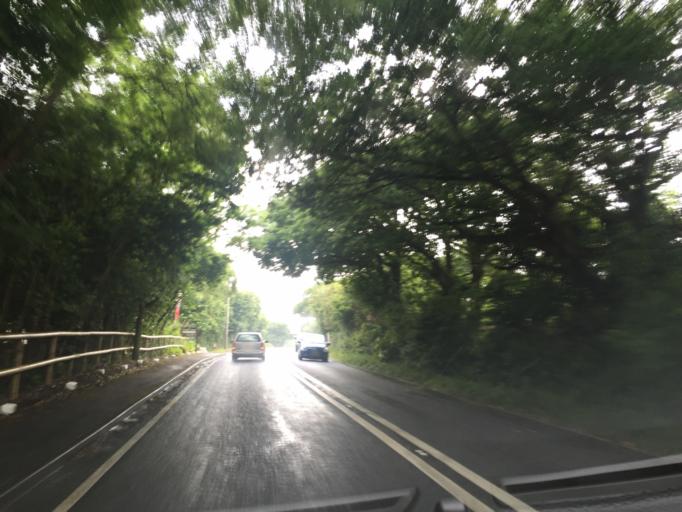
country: GB
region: England
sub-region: Dorset
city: Swanage
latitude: 50.6219
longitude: -2.0170
